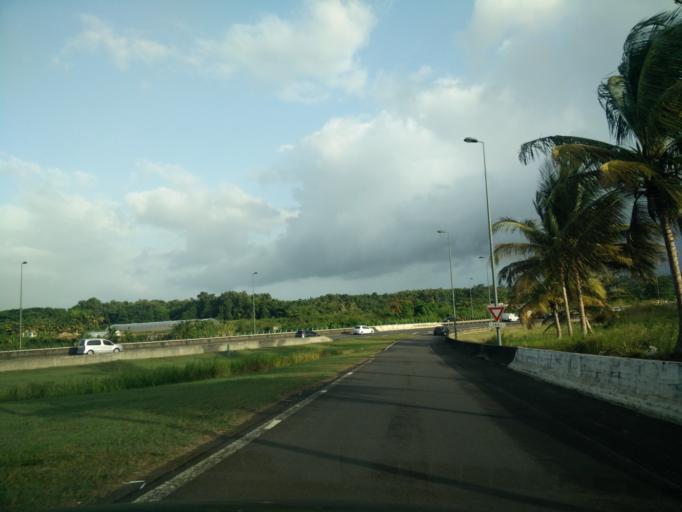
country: GP
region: Guadeloupe
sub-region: Guadeloupe
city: Petit-Bourg
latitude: 16.2170
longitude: -61.6002
